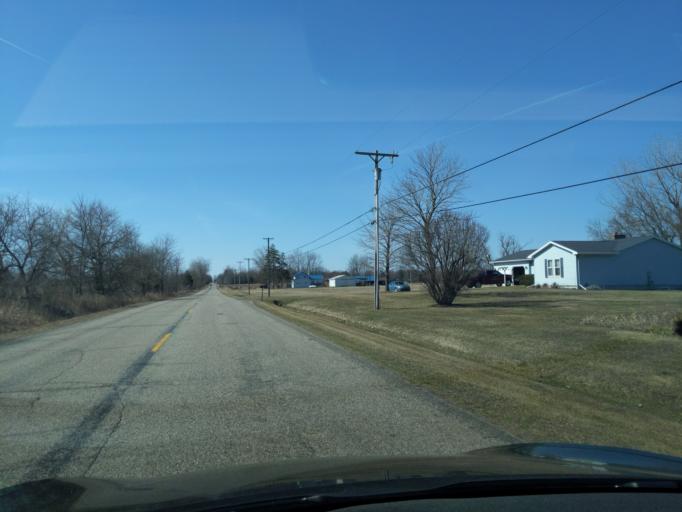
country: US
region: Michigan
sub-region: Eaton County
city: Grand Ledge
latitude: 42.7265
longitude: -84.7703
